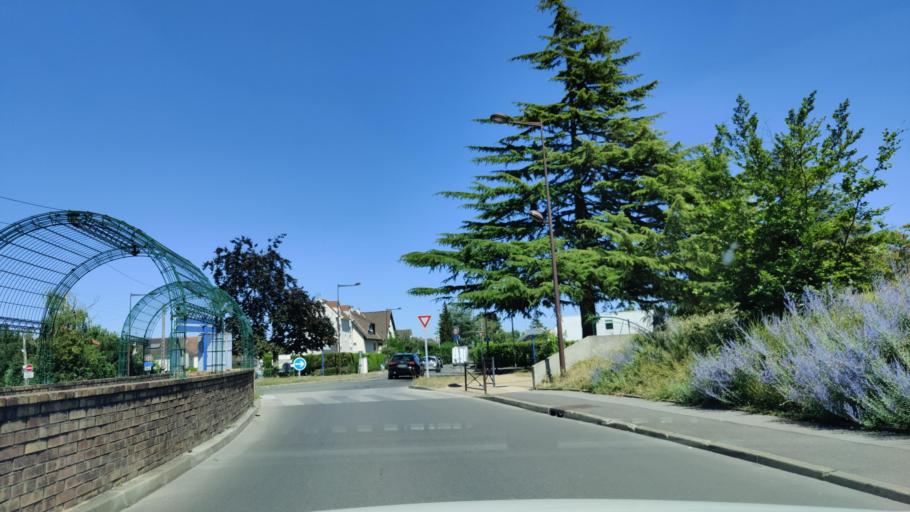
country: FR
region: Ile-de-France
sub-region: Departement de l'Essonne
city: Les Ulis
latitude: 48.6847
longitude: 2.1792
